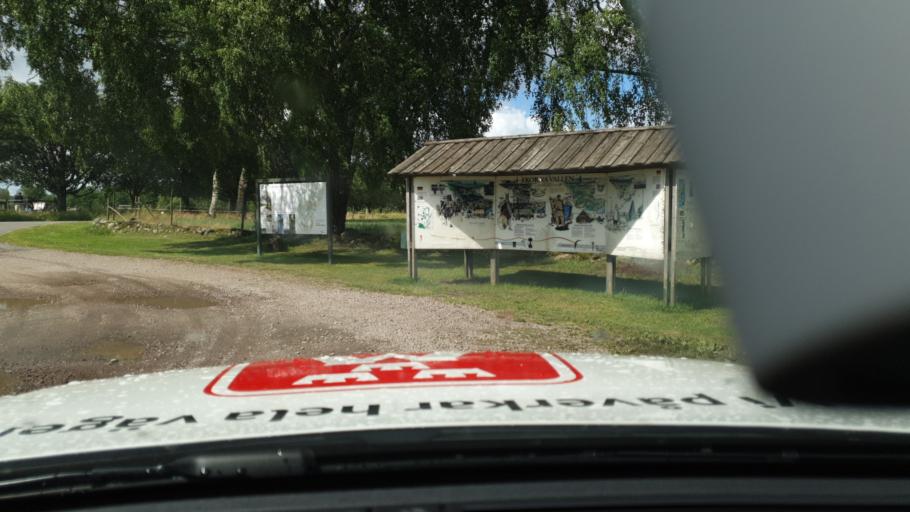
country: SE
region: Vaestra Goetaland
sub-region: Falkopings Kommun
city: Akarp
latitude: 58.2785
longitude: 13.6060
